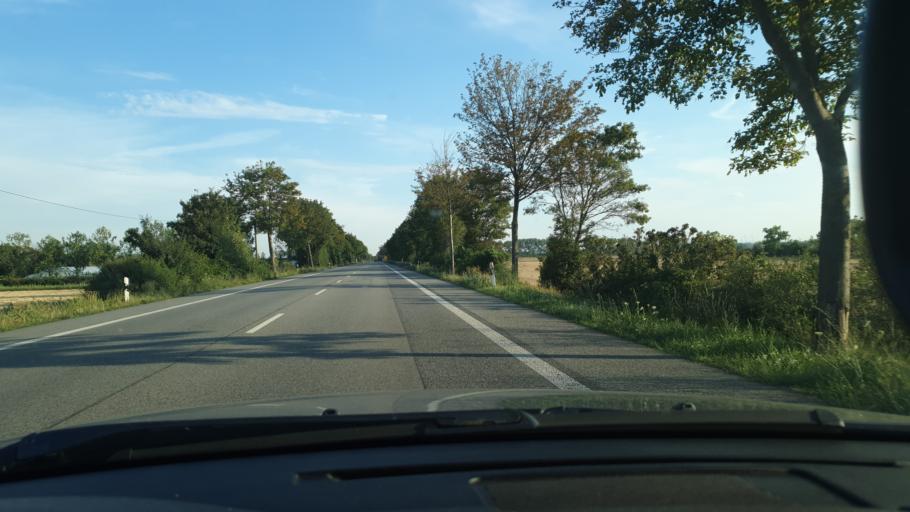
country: DE
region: Rheinland-Pfalz
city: Osthofen
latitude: 49.7206
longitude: 8.3492
